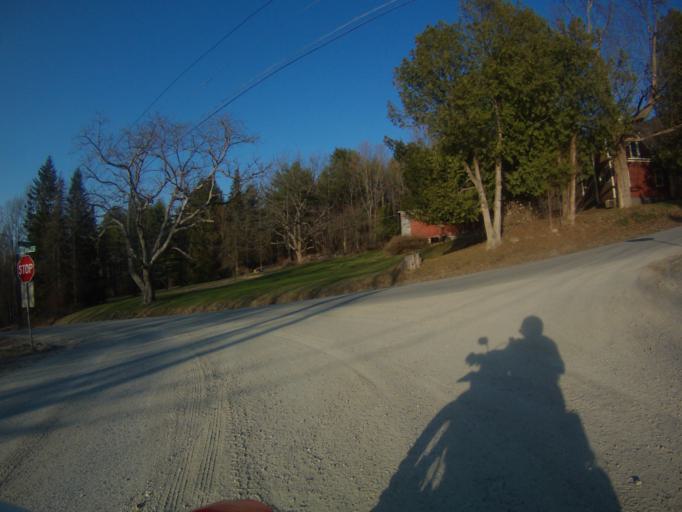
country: US
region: Vermont
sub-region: Addison County
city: Bristol
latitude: 44.1217
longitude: -73.0821
